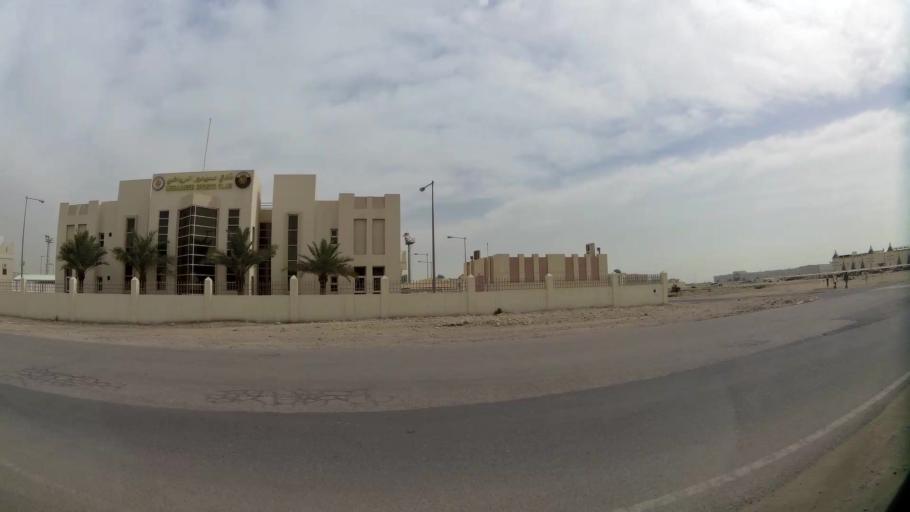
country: QA
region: Baladiyat ad Dawhah
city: Doha
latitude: 25.2208
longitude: 51.4930
